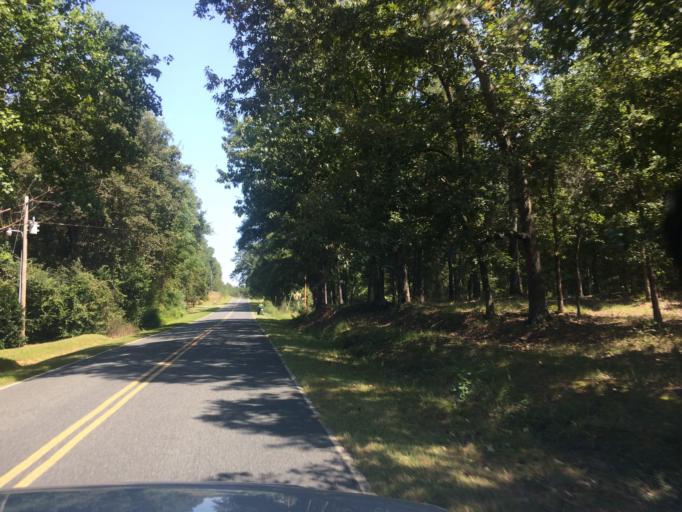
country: US
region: South Carolina
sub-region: Aiken County
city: Aiken
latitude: 33.5319
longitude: -81.5986
